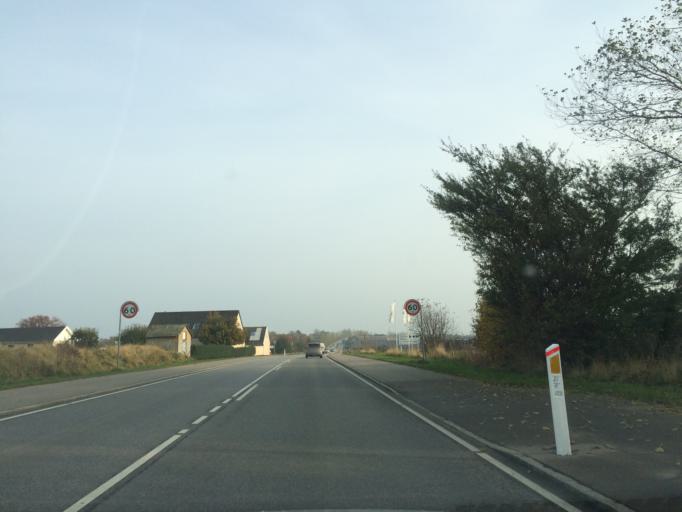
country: DK
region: Zealand
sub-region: Odsherred Kommune
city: Asnaes
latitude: 55.9773
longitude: 11.3312
